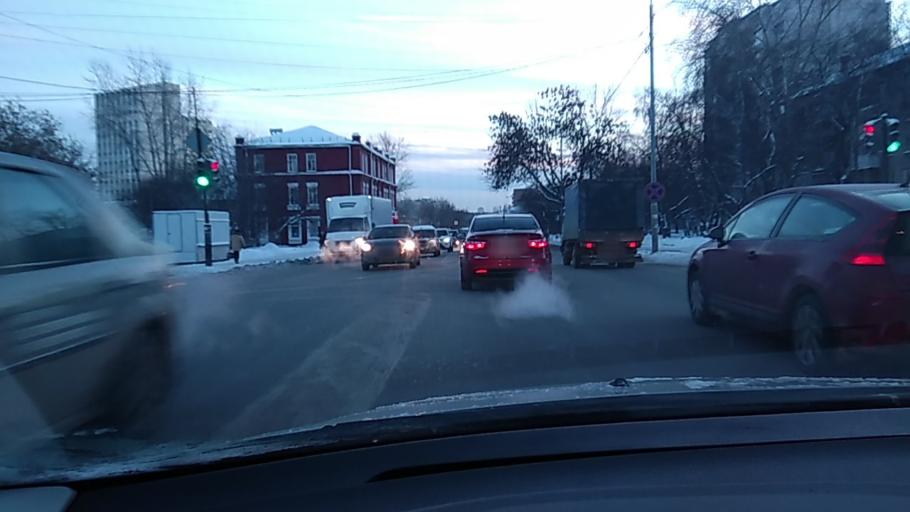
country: RU
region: Sverdlovsk
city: Yekaterinburg
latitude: 56.8237
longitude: 60.6388
